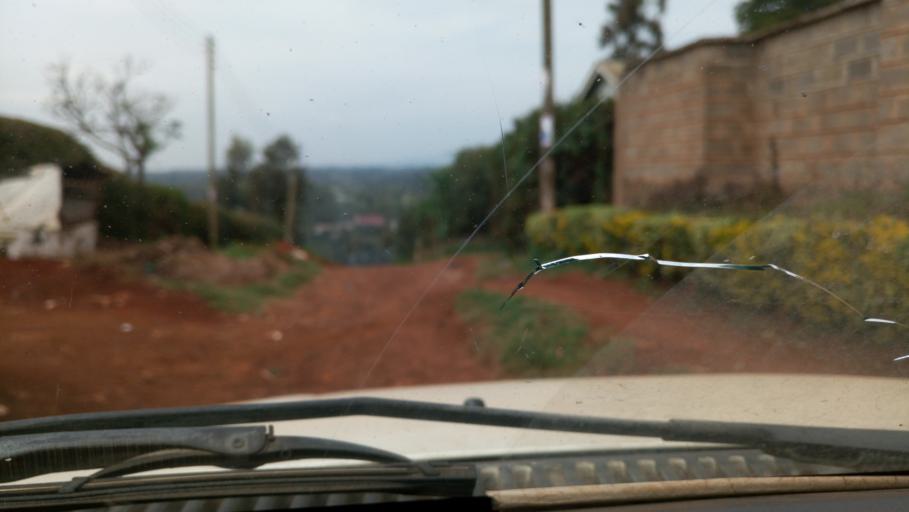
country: KE
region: Kiambu
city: Kikuyu
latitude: -1.2619
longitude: 36.7090
